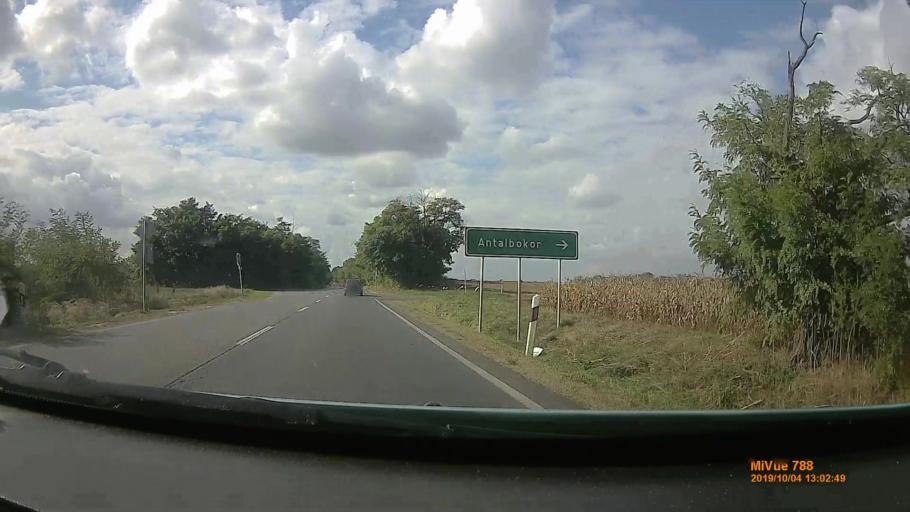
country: HU
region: Szabolcs-Szatmar-Bereg
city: Nyirtelek
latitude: 47.9574
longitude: 21.6459
